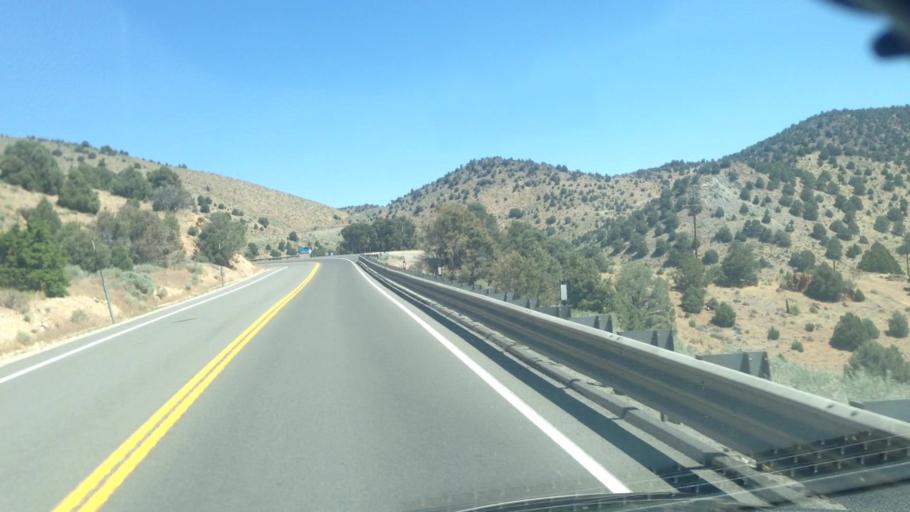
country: US
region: Nevada
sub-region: Storey County
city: Virginia City
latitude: 39.3233
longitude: -119.6441
